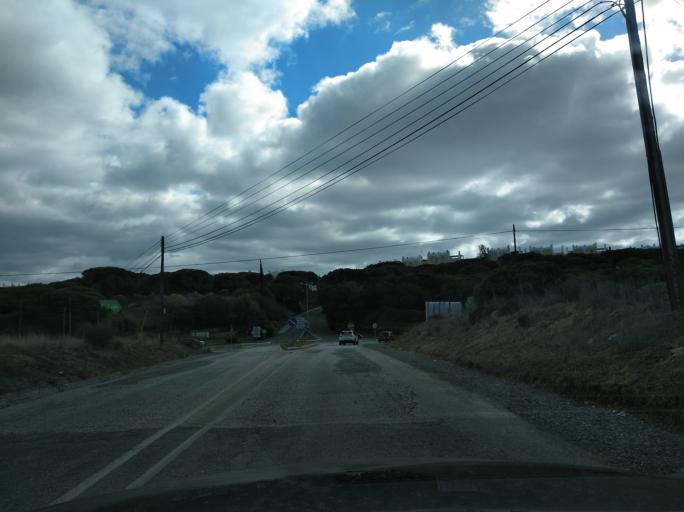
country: PT
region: Faro
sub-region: Vila Real de Santo Antonio
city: Monte Gordo
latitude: 37.1848
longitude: -7.4843
